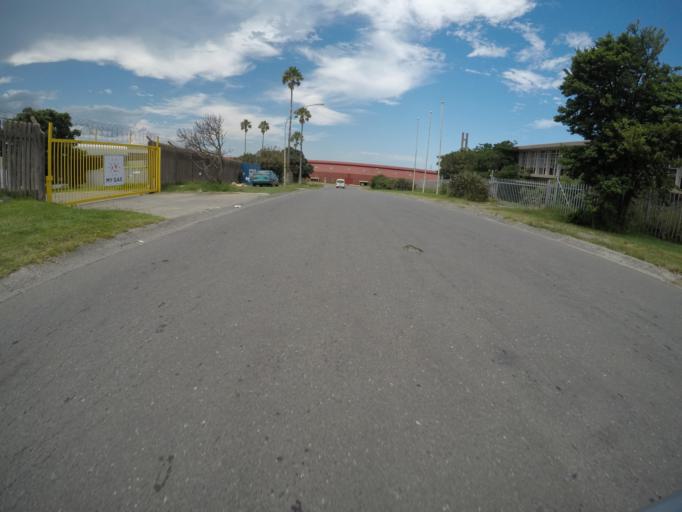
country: ZA
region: Eastern Cape
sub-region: Buffalo City Metropolitan Municipality
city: East London
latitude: -33.0297
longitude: 27.8781
